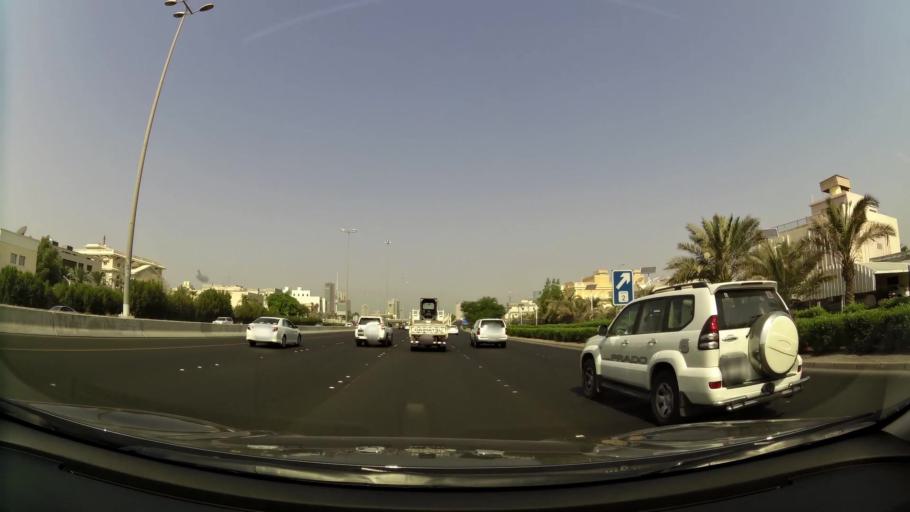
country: KW
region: Al Asimah
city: Ad Dasmah
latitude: 29.3466
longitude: 47.9967
